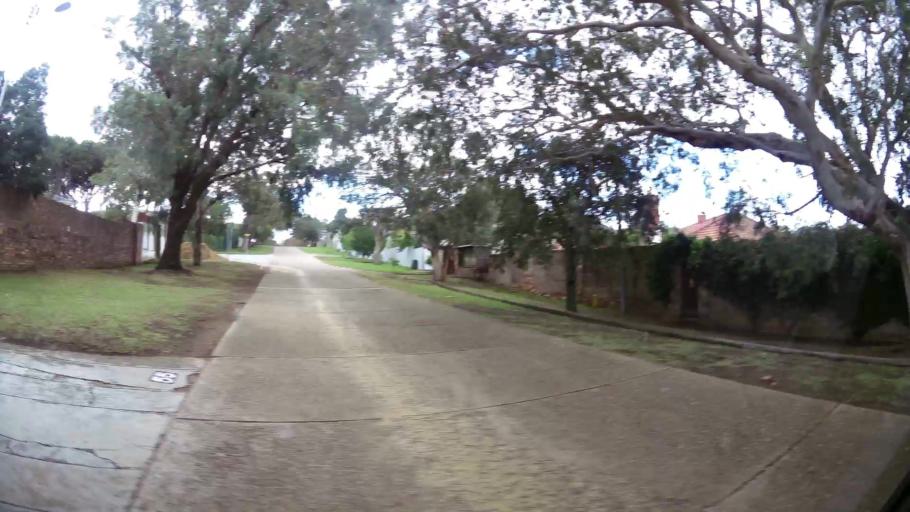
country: ZA
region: Eastern Cape
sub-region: Nelson Mandela Bay Metropolitan Municipality
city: Port Elizabeth
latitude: -33.9669
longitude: 25.5903
